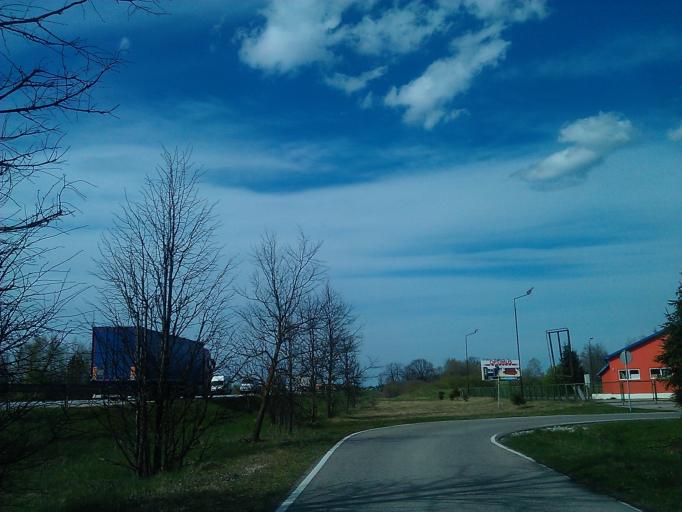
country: LV
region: Adazi
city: Adazi
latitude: 57.0804
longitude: 24.3165
